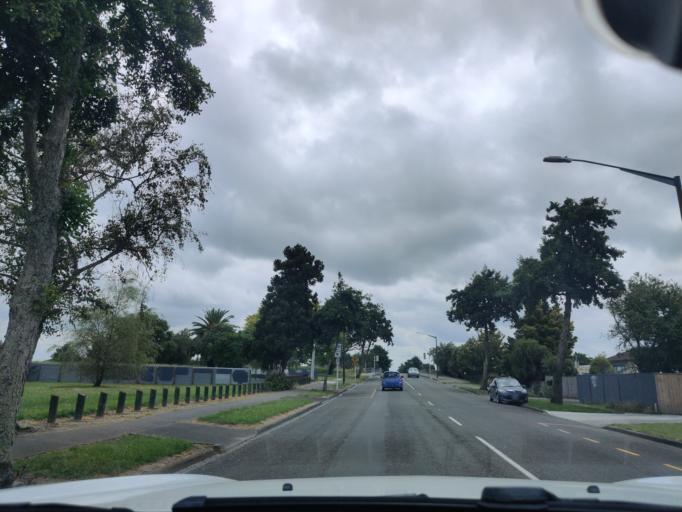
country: NZ
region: Manawatu-Wanganui
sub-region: Palmerston North City
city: Palmerston North
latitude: -40.3543
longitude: 175.5874
